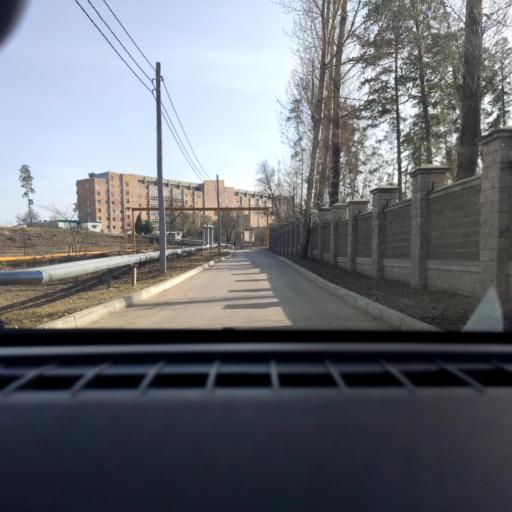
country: RU
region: Samara
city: Tol'yatti
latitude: 53.5006
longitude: 49.3588
